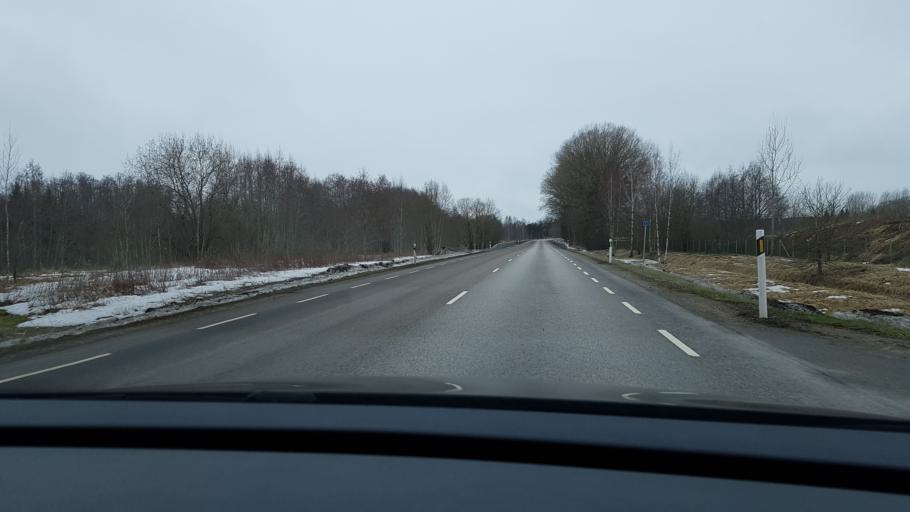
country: EE
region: Paernumaa
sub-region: Sauga vald
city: Sauga
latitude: 58.4375
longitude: 24.4562
